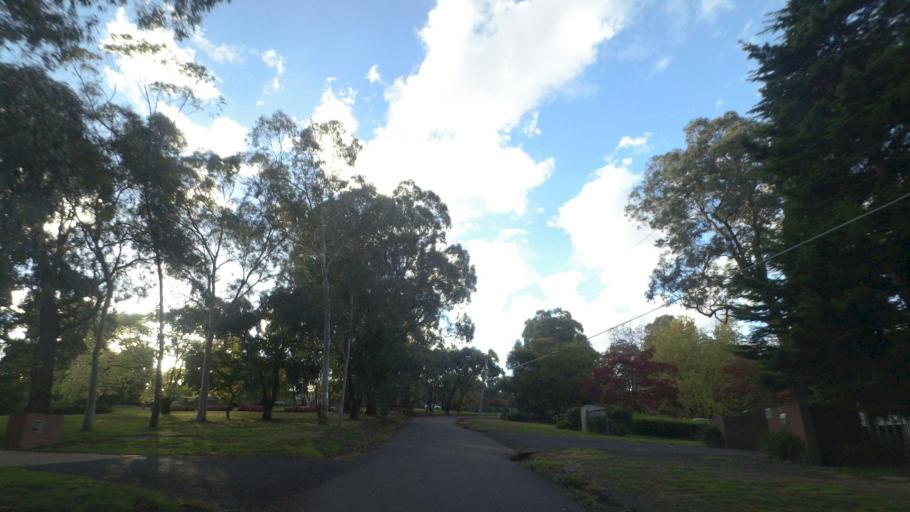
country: AU
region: Victoria
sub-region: Banyule
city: Lower Plenty
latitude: -37.7348
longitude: 145.1267
